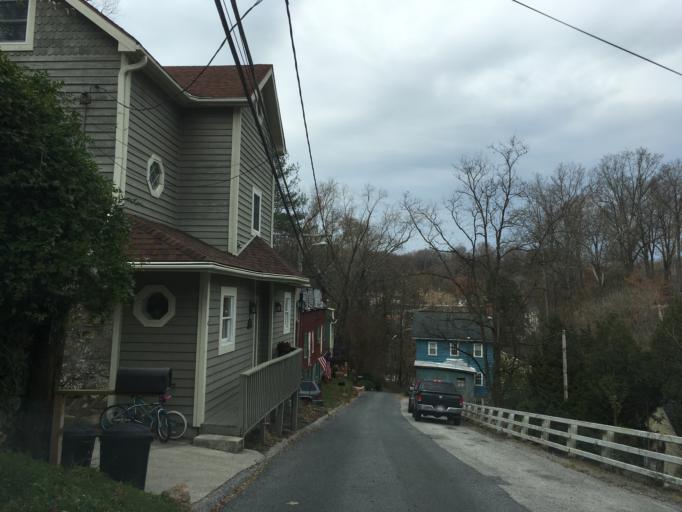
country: US
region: Maryland
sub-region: Howard County
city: Ellicott City
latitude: 39.2733
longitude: -76.7855
